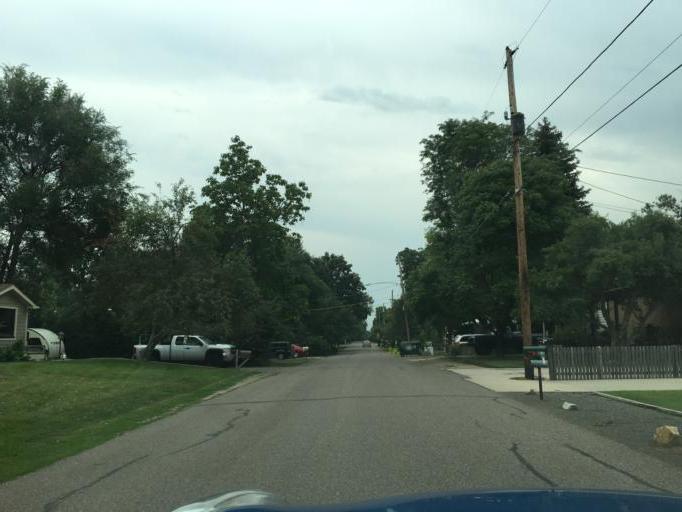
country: US
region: Colorado
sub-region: Jefferson County
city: Wheat Ridge
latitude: 39.7538
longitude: -105.1001
